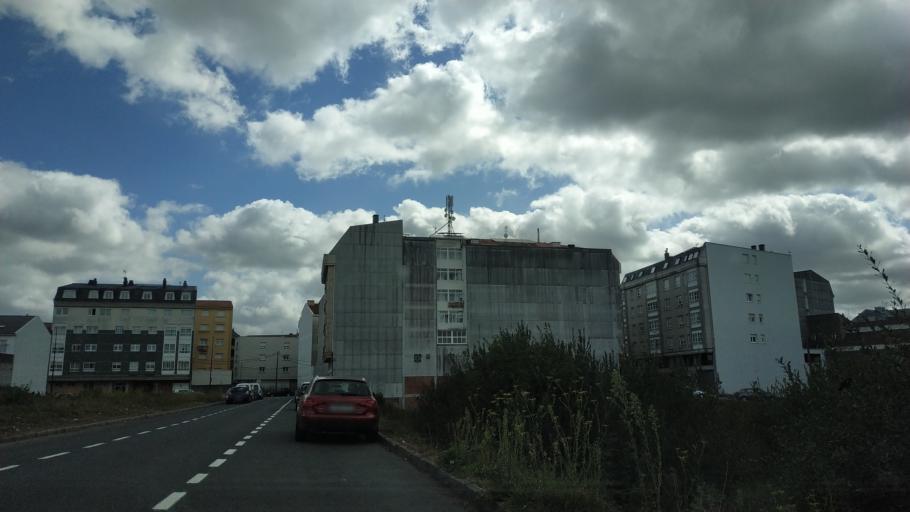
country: ES
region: Galicia
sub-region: Provincia da Coruna
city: Carballo
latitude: 43.2212
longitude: -8.6872
